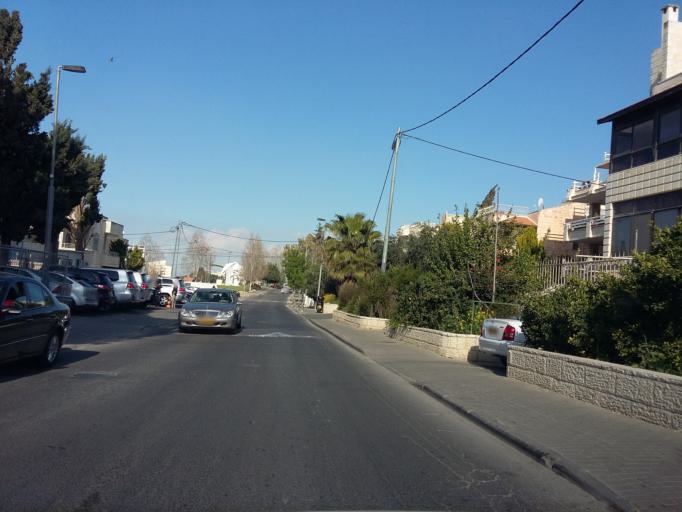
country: PS
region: West Bank
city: East Jerusalem
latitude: 31.7997
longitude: 35.2357
